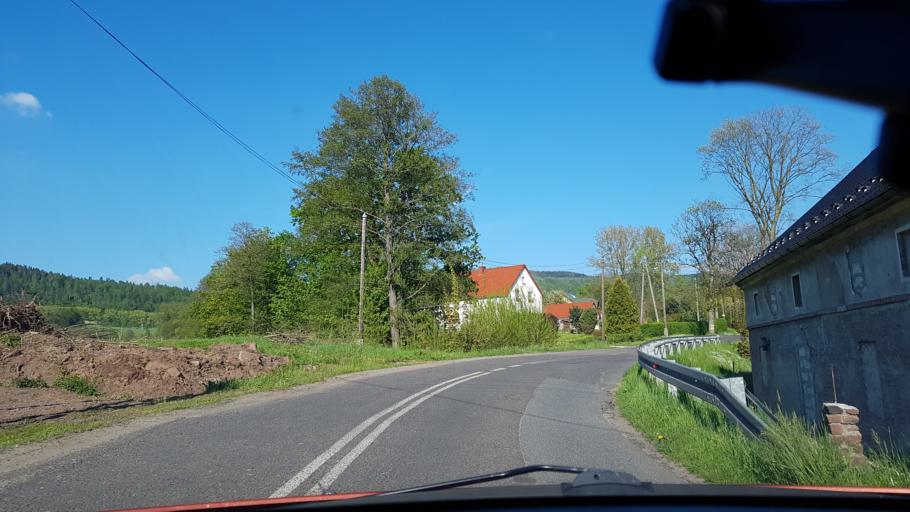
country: PL
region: Lower Silesian Voivodeship
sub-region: Powiat klodzki
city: Jugow
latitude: 50.5895
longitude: 16.5611
